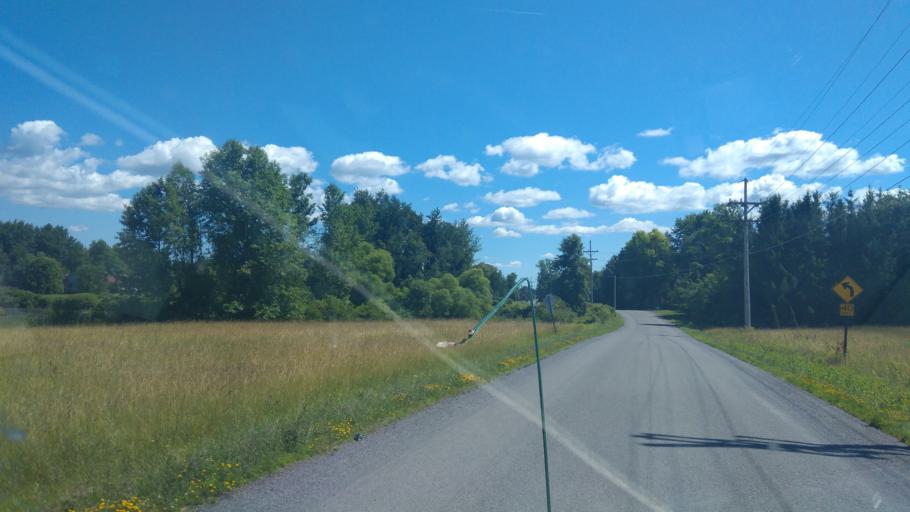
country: US
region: New York
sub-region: Wayne County
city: Sodus
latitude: 43.2178
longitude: -77.0258
